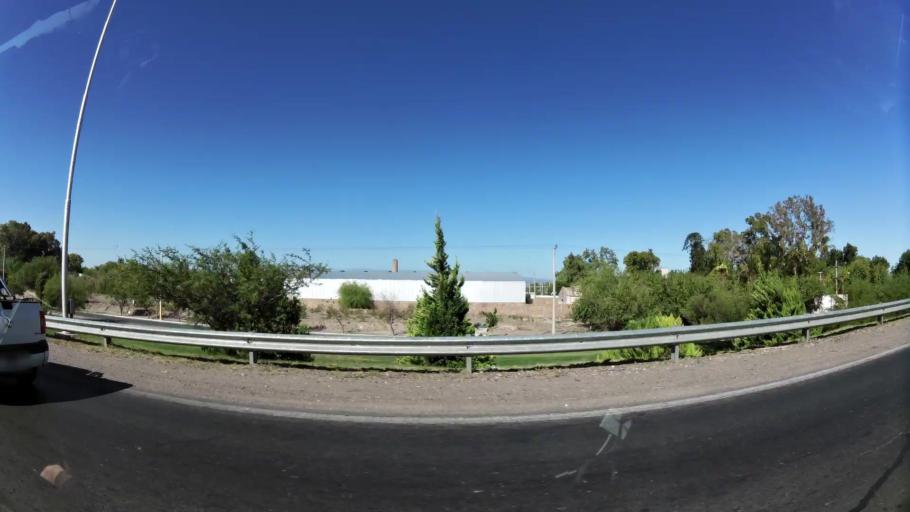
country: AR
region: San Juan
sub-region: Departamento de Santa Lucia
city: Santa Lucia
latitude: -31.5325
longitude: -68.5040
